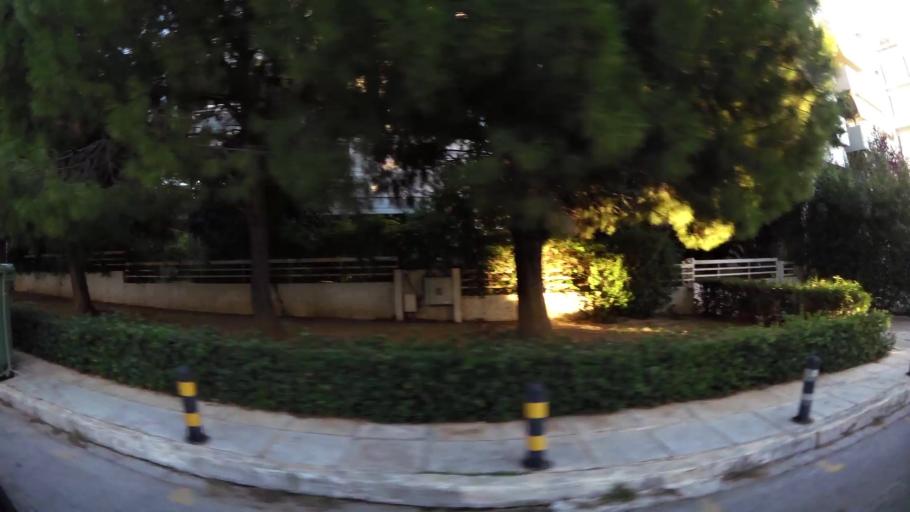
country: GR
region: Attica
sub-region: Nomarchia Athinas
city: Glyfada
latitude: 37.8777
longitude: 23.7526
